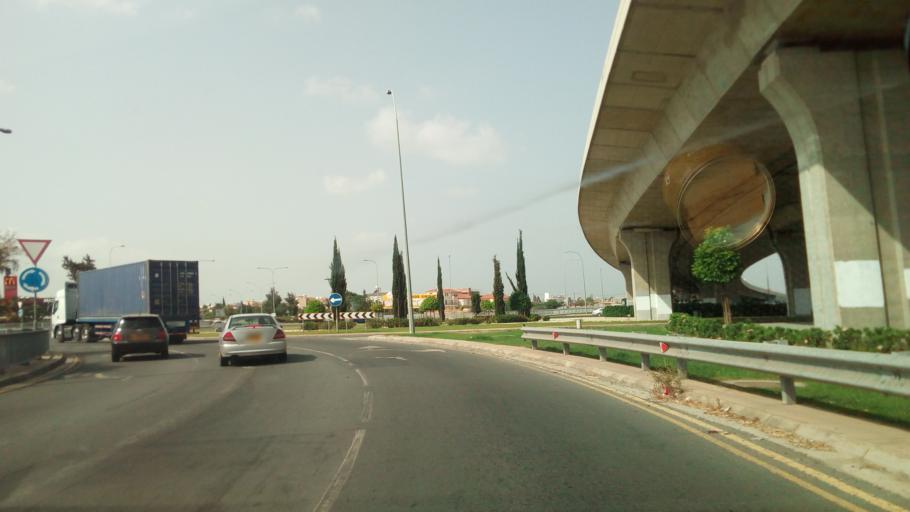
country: CY
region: Limassol
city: Pano Polemidia
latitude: 34.6897
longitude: 33.0094
